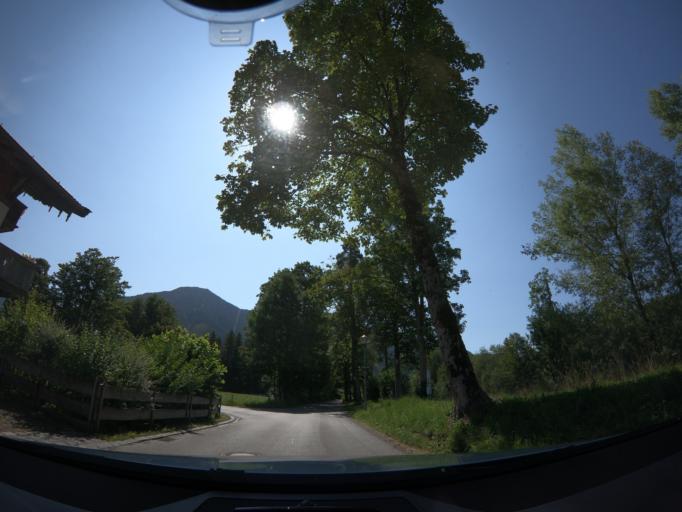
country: DE
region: Bavaria
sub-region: Upper Bavaria
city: Rottach-Egern
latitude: 47.6826
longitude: 11.7651
